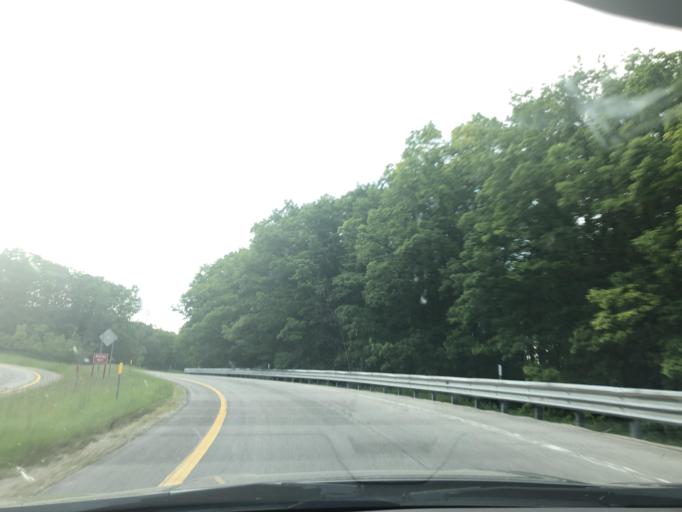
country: US
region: Michigan
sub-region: Clare County
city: Harrison
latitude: 43.9917
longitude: -84.7738
